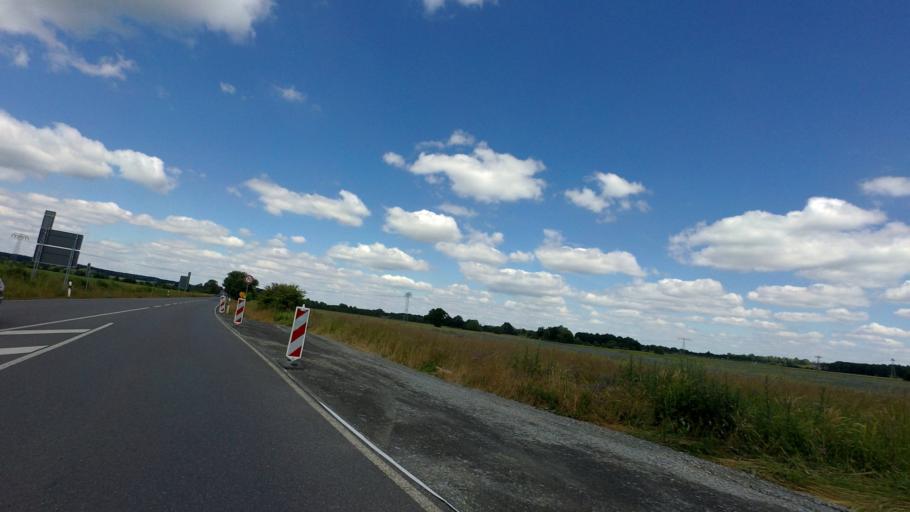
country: DE
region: Brandenburg
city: Grossraschen
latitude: 51.5855
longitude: 13.9524
